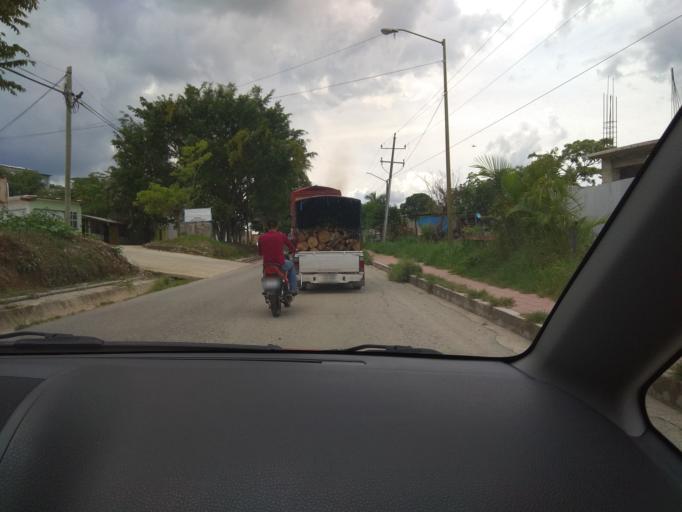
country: MX
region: Chiapas
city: Ocosingo
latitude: 16.8990
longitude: -92.0793
